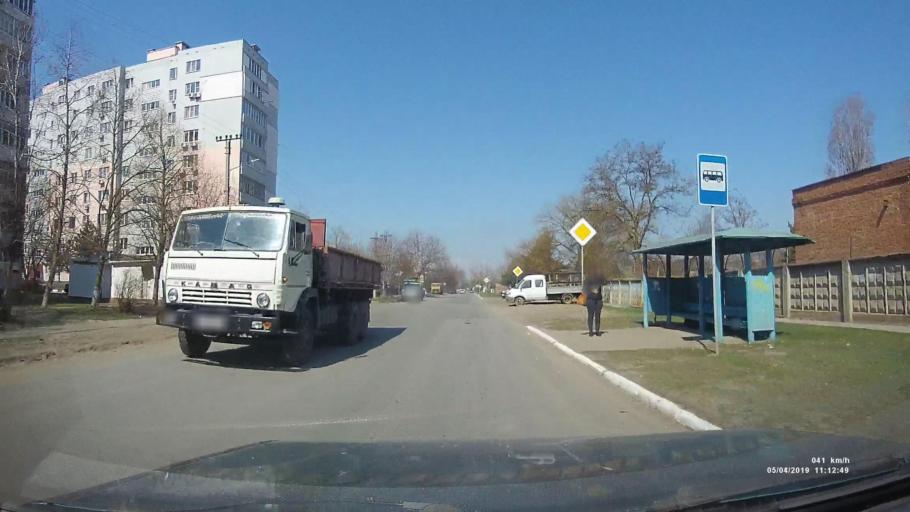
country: RU
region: Rostov
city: Azov
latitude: 47.0996
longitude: 39.4350
